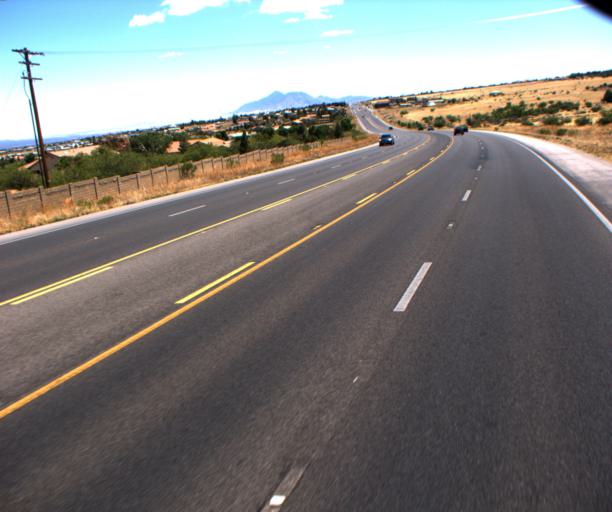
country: US
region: Arizona
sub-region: Cochise County
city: Sierra Vista Southeast
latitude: 31.4455
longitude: -110.2564
